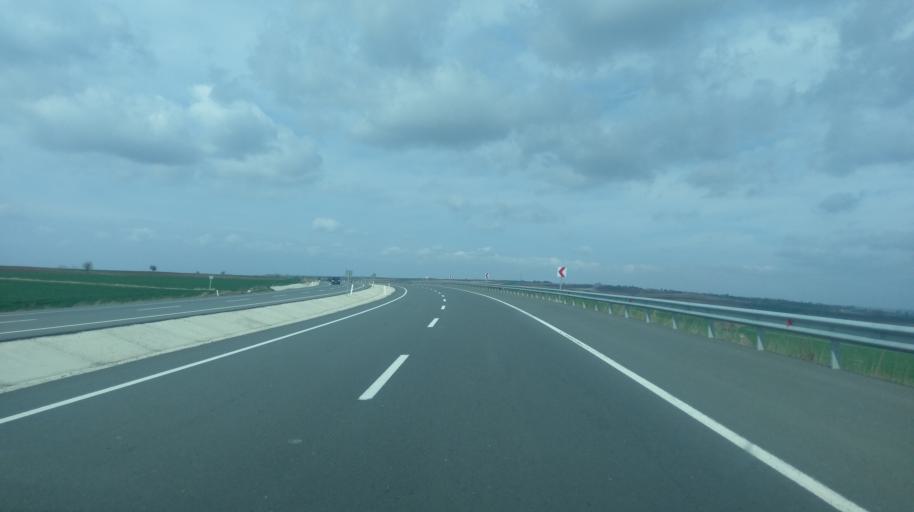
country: TR
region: Edirne
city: Hamidiye
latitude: 41.0331
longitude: 26.6353
